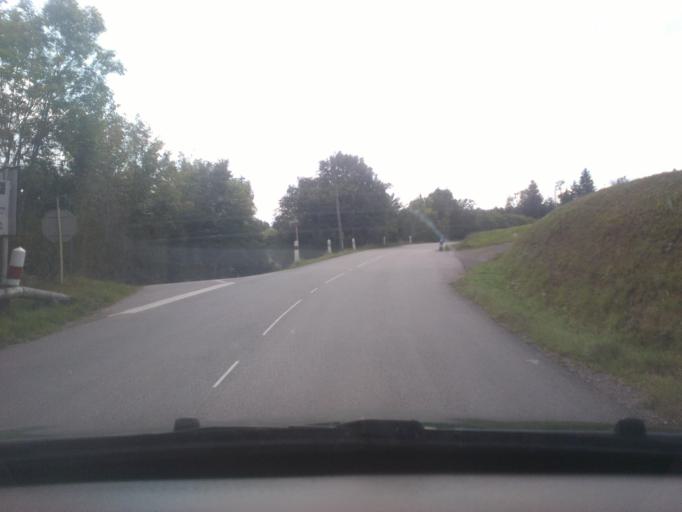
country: FR
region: Lorraine
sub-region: Departement des Vosges
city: Corcieux
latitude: 48.1652
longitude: 6.8731
